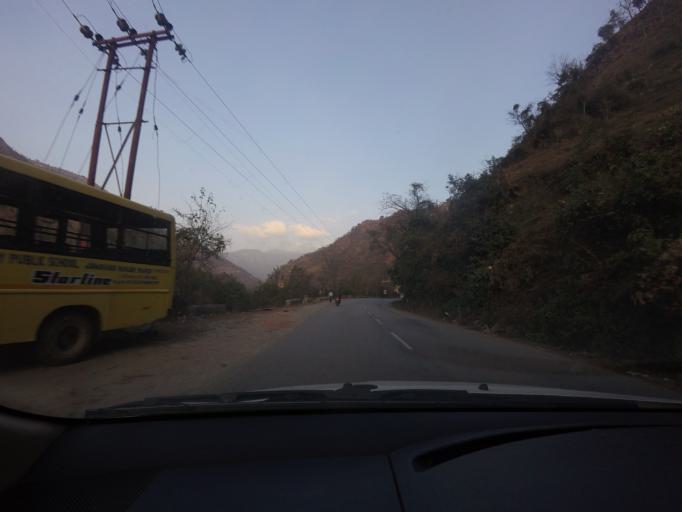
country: IN
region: Himachal Pradesh
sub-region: Mandi
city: Mandi
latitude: 31.7019
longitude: 76.9724
